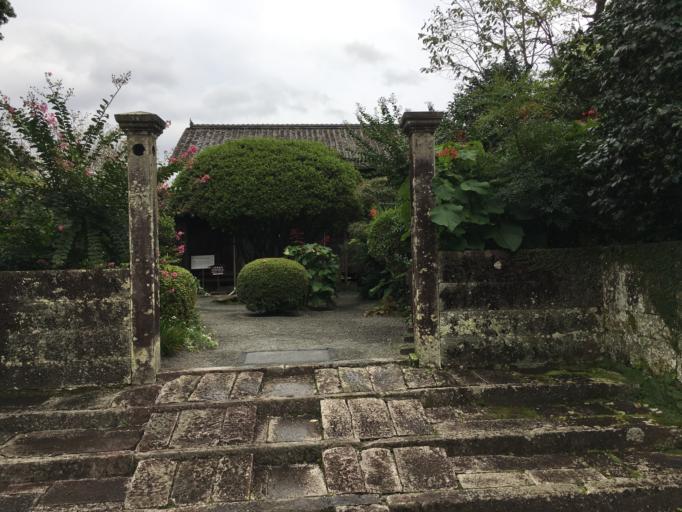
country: JP
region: Miyazaki
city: Nichinan
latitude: 31.6272
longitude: 131.3520
